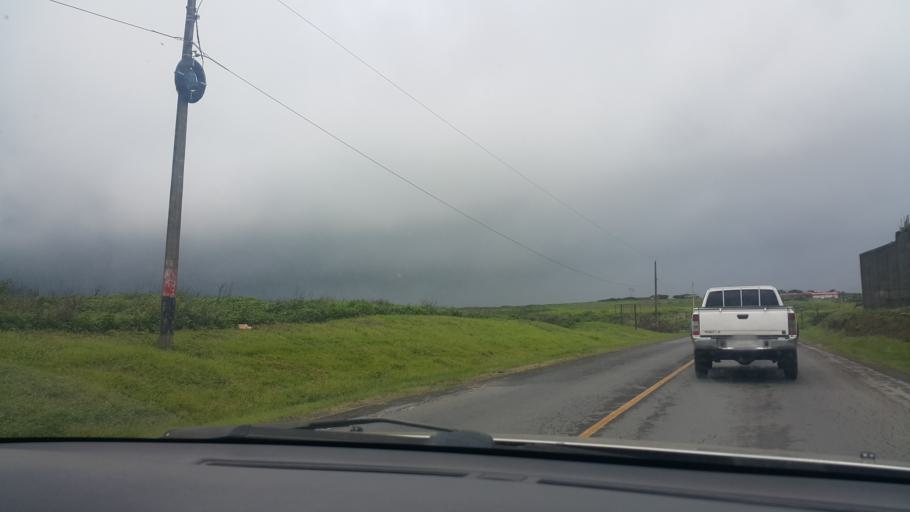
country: NI
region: Managua
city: El Crucero
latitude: 11.9444
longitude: -86.2987
